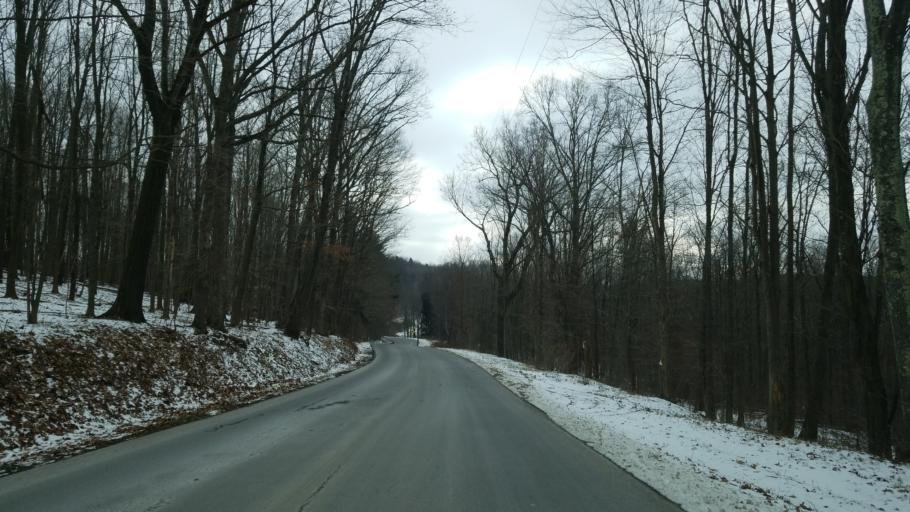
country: US
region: Pennsylvania
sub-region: Clearfield County
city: Sandy
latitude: 41.0929
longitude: -78.7508
